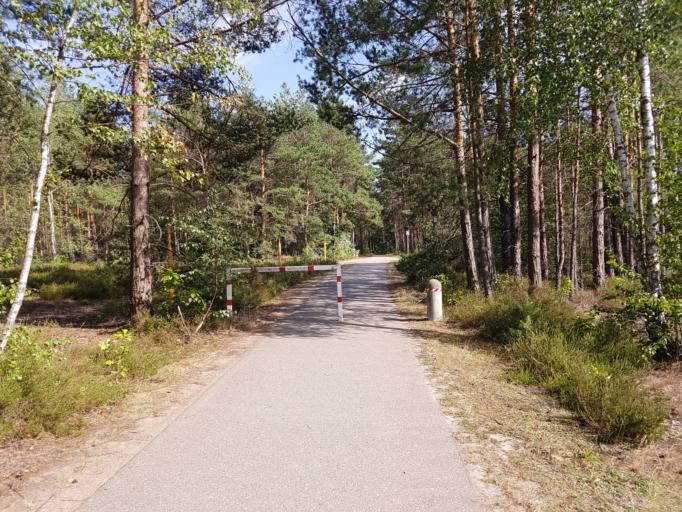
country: DE
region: Brandenburg
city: Finsterwalde
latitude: 51.6240
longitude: 13.6656
